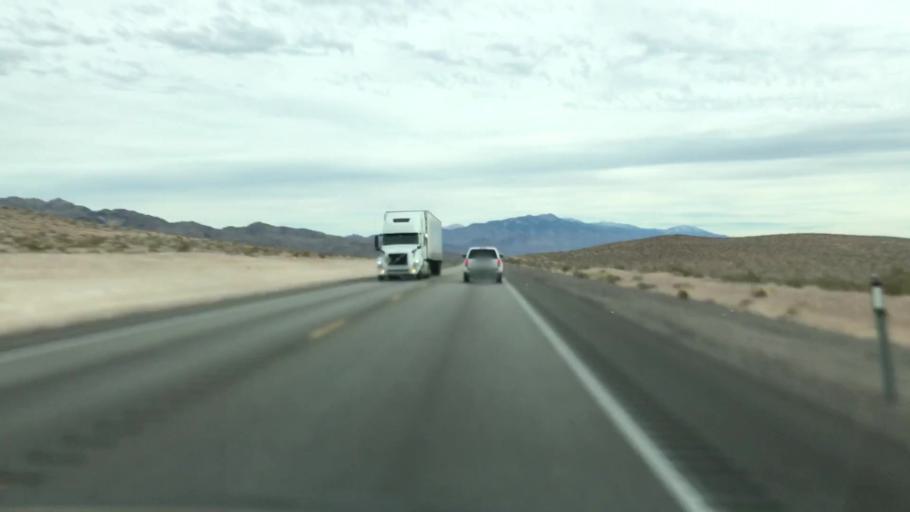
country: US
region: Nevada
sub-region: Nye County
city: Pahrump
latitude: 36.6131
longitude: -116.2766
